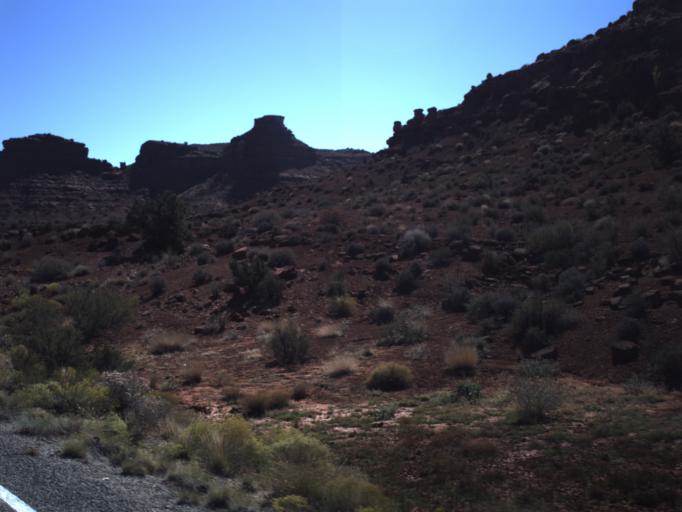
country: US
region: Utah
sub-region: San Juan County
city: Blanding
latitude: 37.8099
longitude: -110.3313
